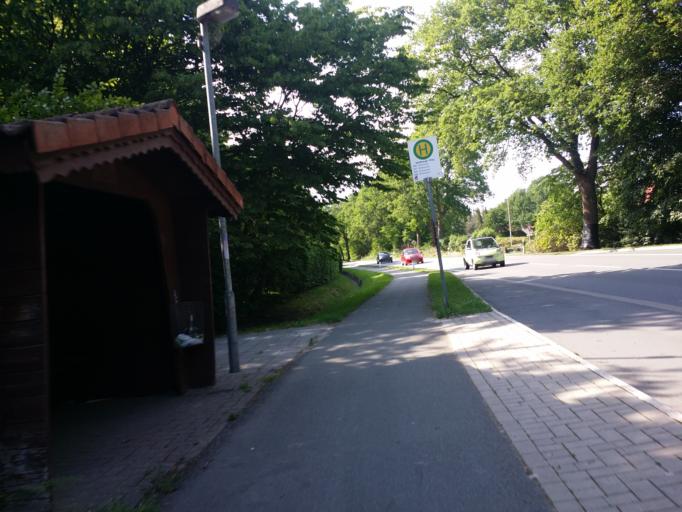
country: DE
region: Lower Saxony
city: Wiefelstede
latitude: 53.2804
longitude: 8.1067
